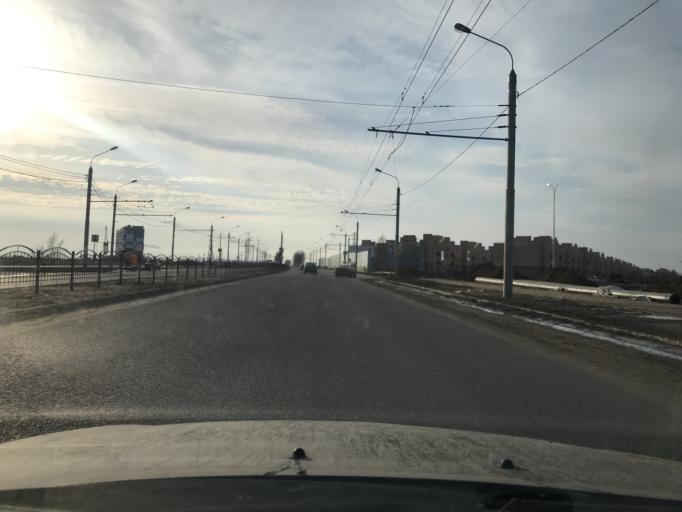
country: RU
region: Kaluga
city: Mstikhino
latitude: 54.4911
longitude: 36.1840
